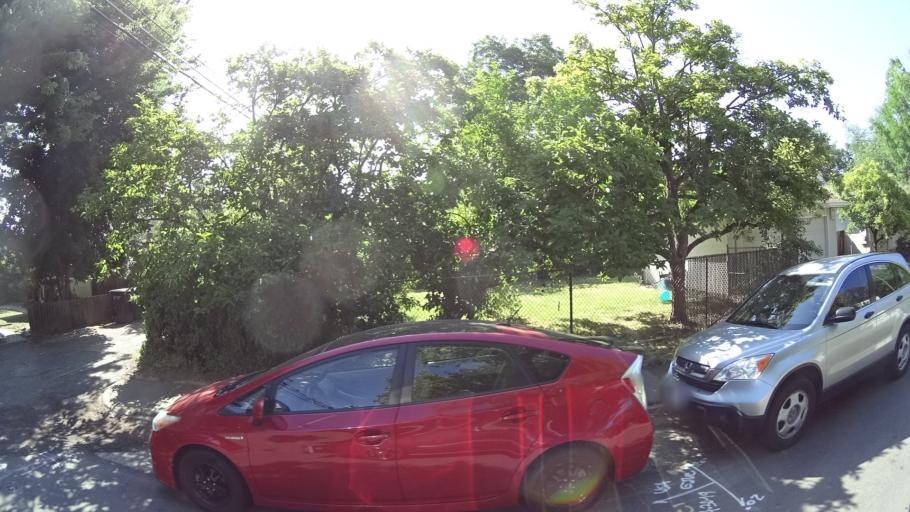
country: US
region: California
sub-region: Sacramento County
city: Sacramento
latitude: 38.5562
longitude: -121.4483
